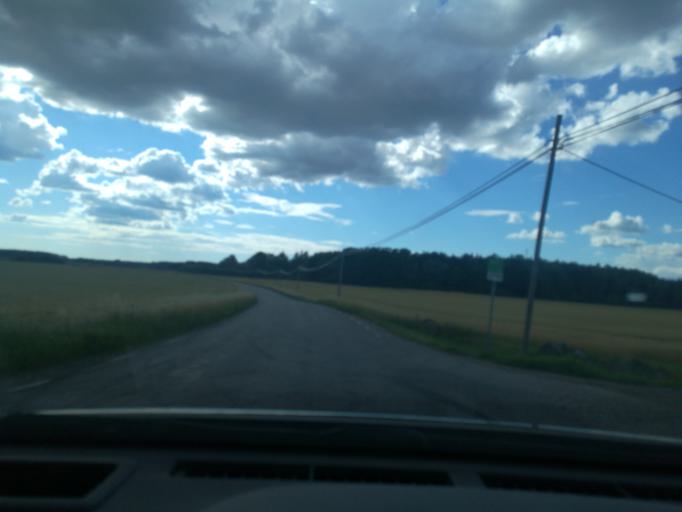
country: SE
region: Soedermanland
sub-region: Eskilstuna Kommun
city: Arla
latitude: 59.4480
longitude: 16.7561
